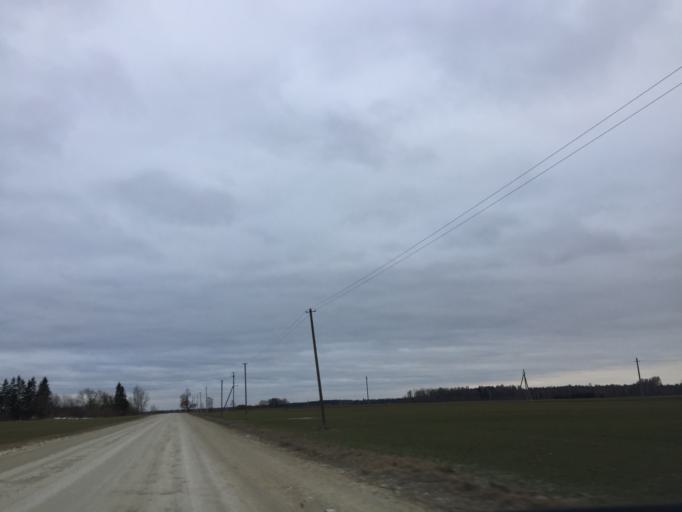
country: LT
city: Zagare
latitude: 56.3358
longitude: 23.2468
